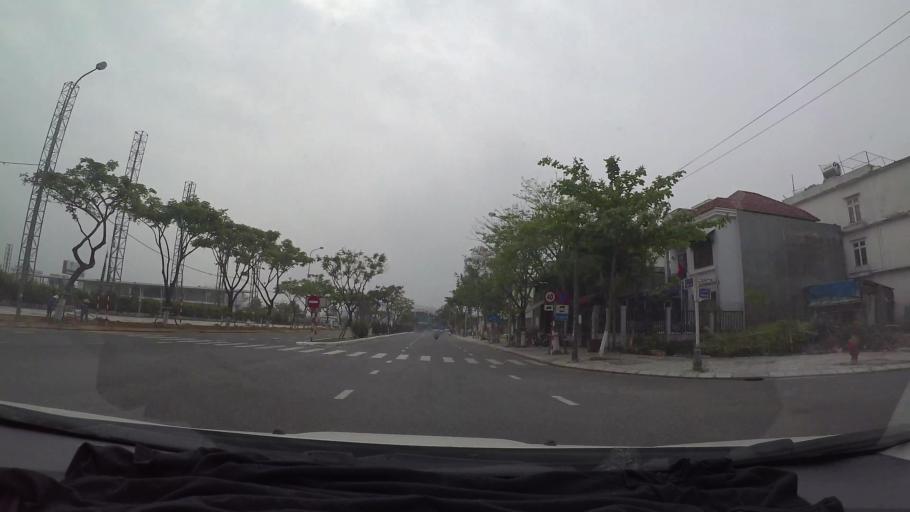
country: VN
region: Da Nang
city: Cam Le
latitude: 16.0251
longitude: 108.2153
